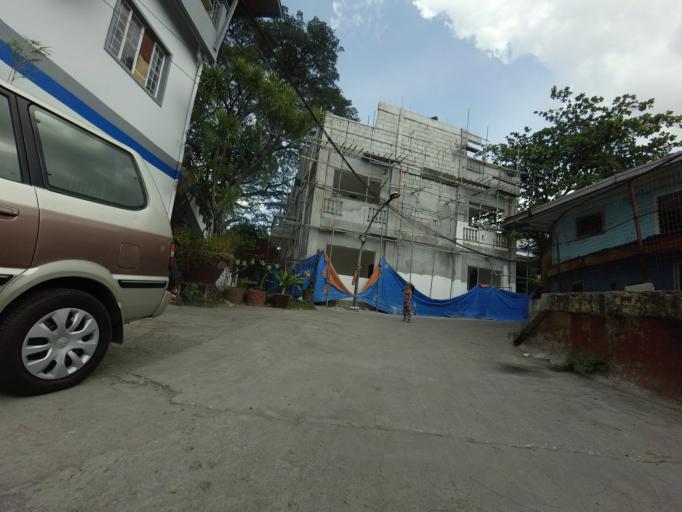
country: PH
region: Calabarzon
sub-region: Province of Rizal
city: Pateros
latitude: 14.5612
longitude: 121.0734
